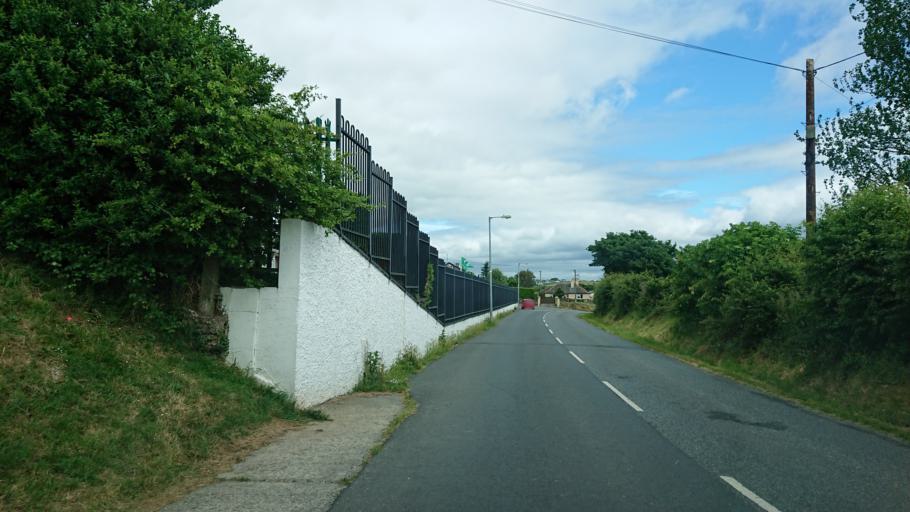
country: IE
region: Munster
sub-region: Waterford
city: Dunmore East
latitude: 52.2310
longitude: -6.9738
